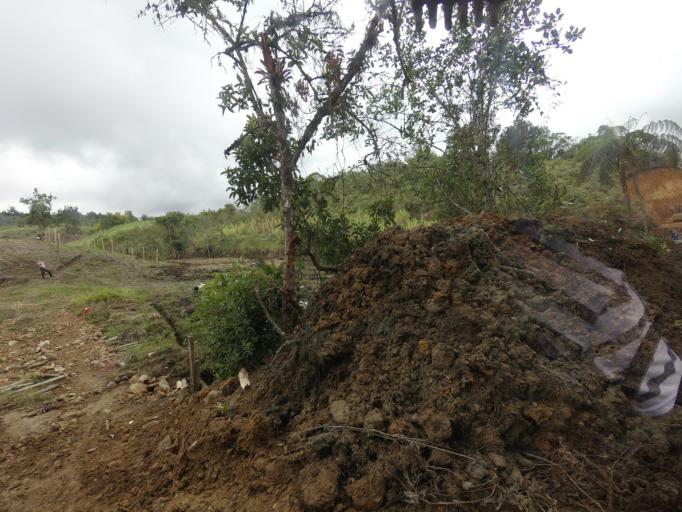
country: CO
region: Huila
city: San Agustin
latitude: 1.9508
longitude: -76.2969
